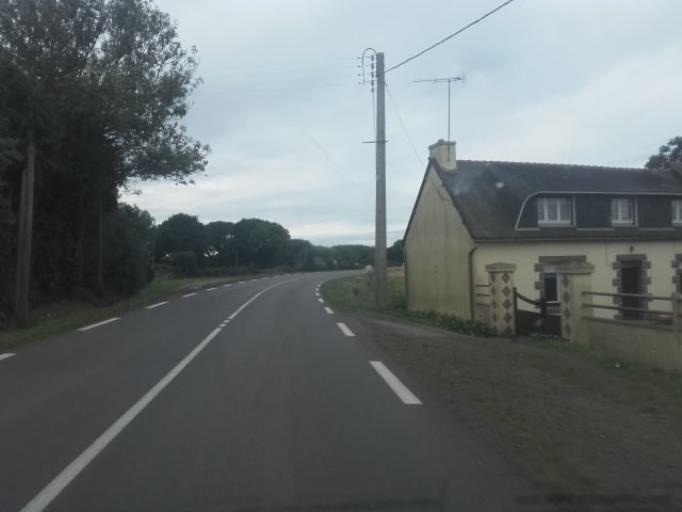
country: FR
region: Brittany
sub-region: Departement des Cotes-d'Armor
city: Pleguien
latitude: 48.5991
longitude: -2.9536
